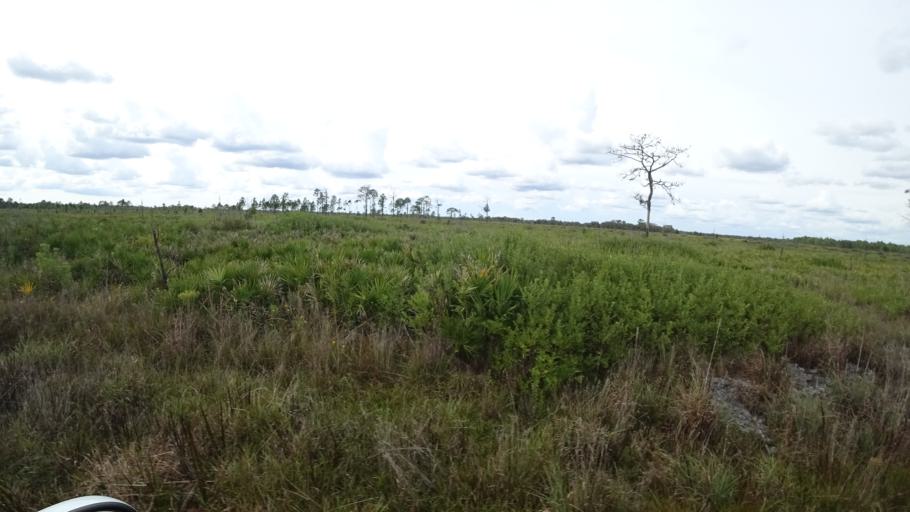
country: US
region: Florida
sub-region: Hillsborough County
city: Wimauma
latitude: 27.5564
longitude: -82.1316
